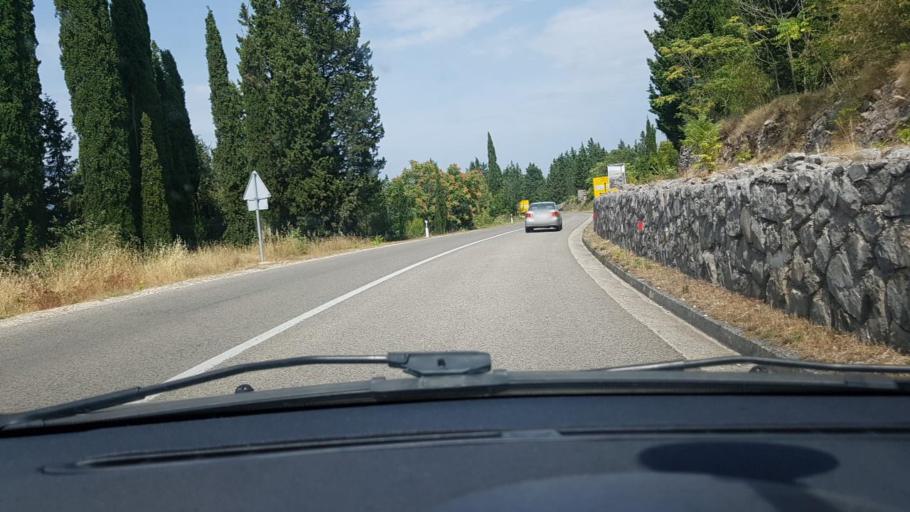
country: HR
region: Dubrovacko-Neretvanska
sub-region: Grad Korcula
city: Zrnovo
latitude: 42.9435
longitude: 17.1056
